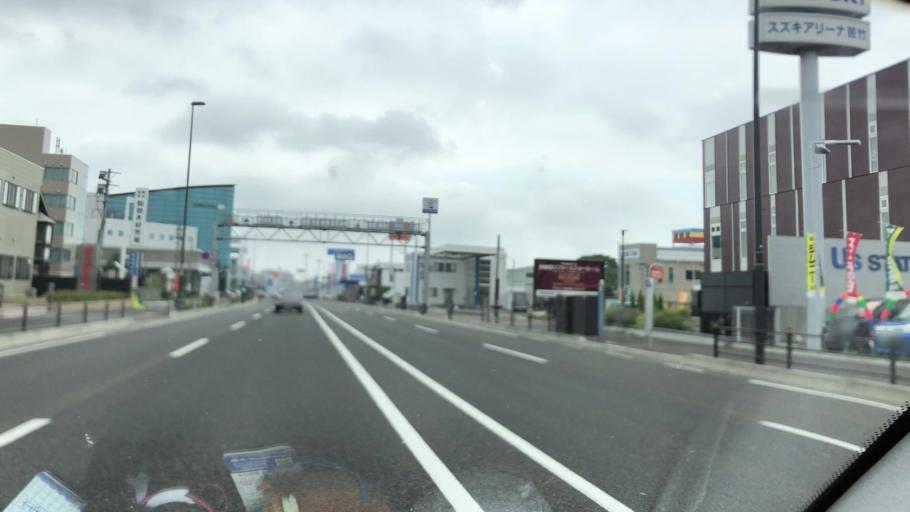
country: JP
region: Miyagi
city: Sendai-shi
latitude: 38.2695
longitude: 140.9269
